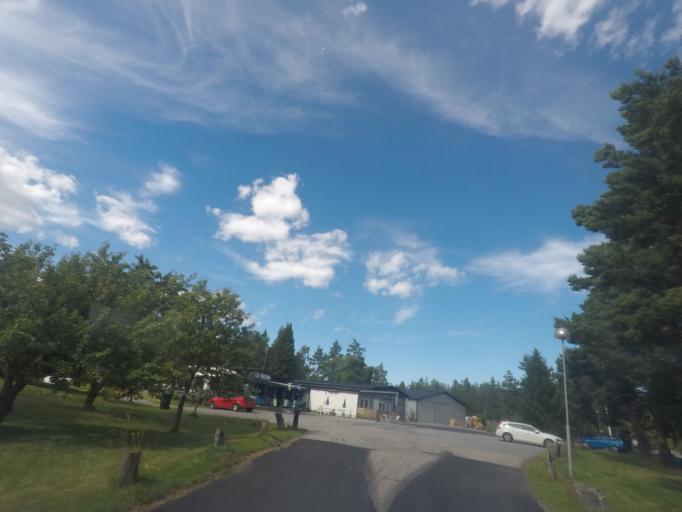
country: SE
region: Stockholm
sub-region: Norrtalje Kommun
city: Arno
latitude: 60.0924
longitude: 18.7937
